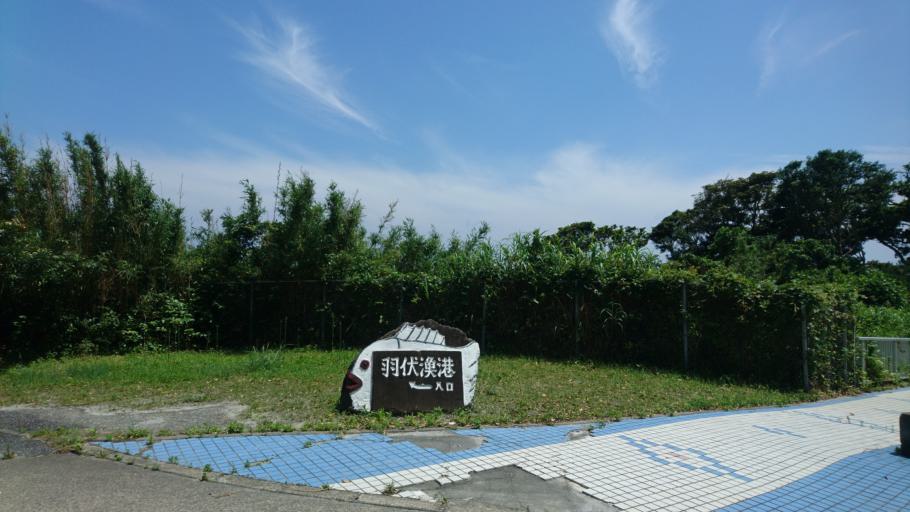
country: JP
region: Shizuoka
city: Shimoda
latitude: 34.3898
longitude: 139.2759
